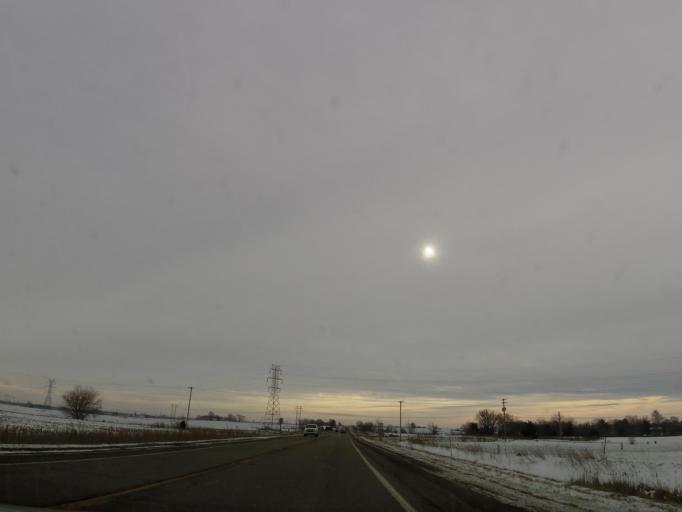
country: US
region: Illinois
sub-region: LaSalle County
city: Oglesby
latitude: 41.2929
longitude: -89.0987
